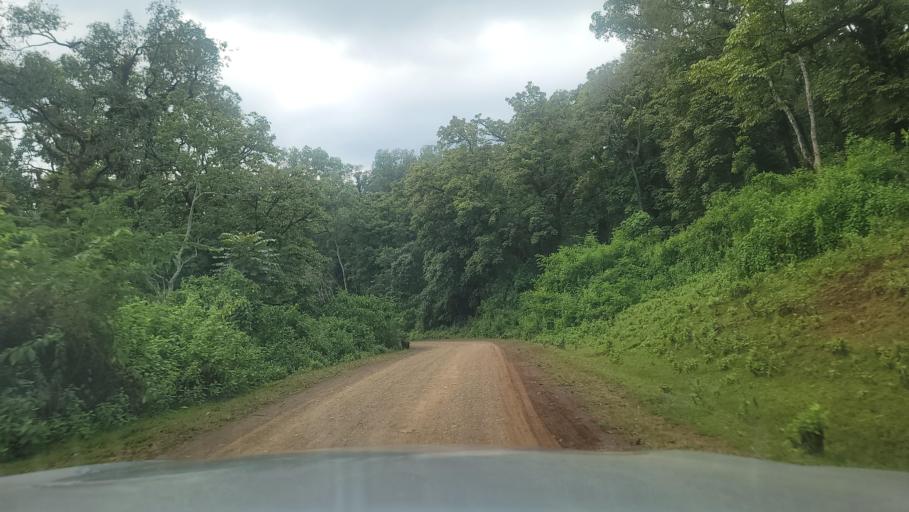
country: ET
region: Oromiya
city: Agaro
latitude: 7.7100
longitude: 36.2538
